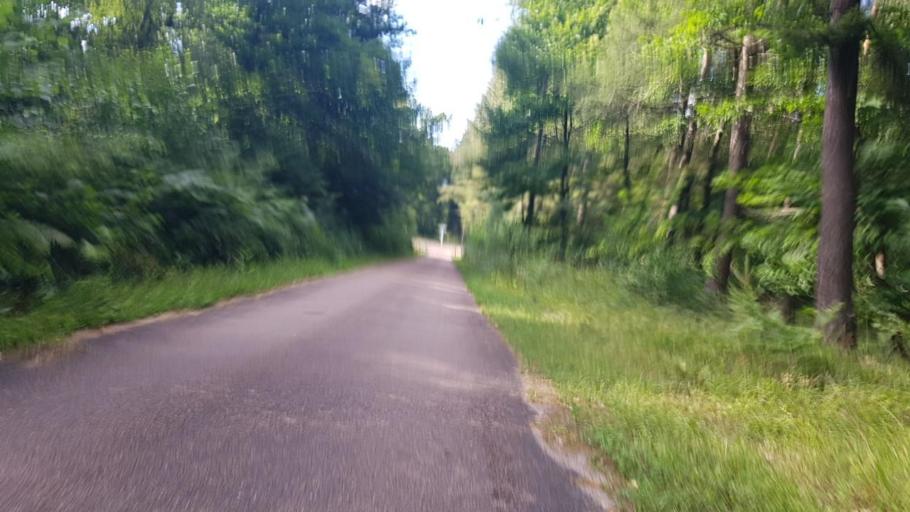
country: FR
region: Picardie
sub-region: Departement de l'Oise
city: Chamant
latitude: 49.1696
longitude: 2.6322
